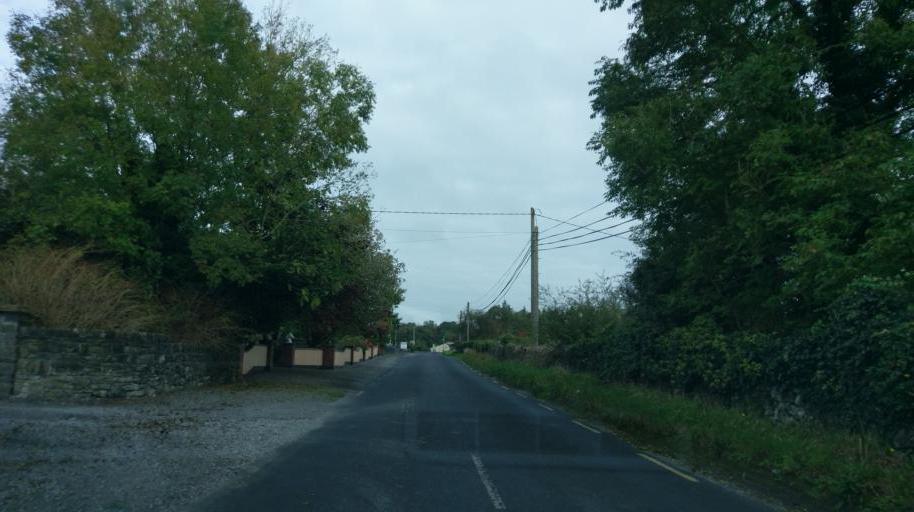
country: IE
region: Connaught
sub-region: County Galway
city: Athenry
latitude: 53.3700
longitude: -8.7012
